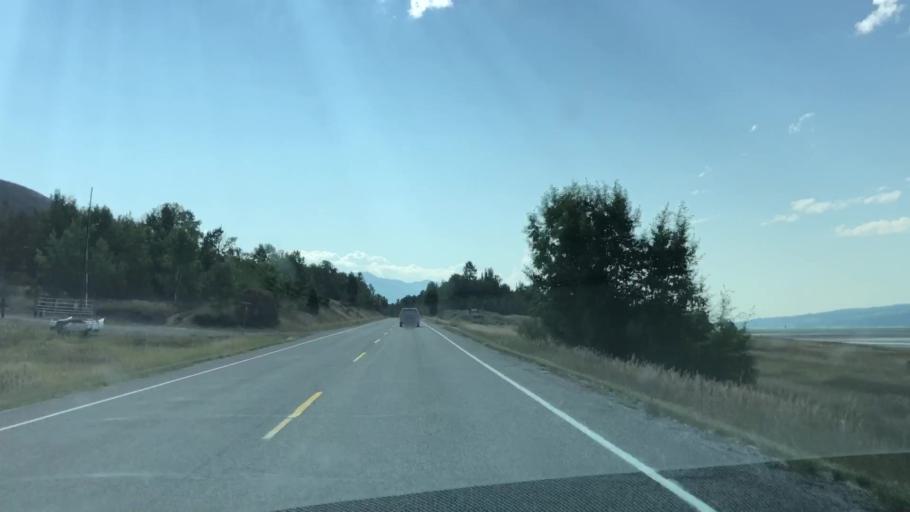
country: US
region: Wyoming
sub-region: Teton County
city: Hoback
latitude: 43.2133
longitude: -111.0613
